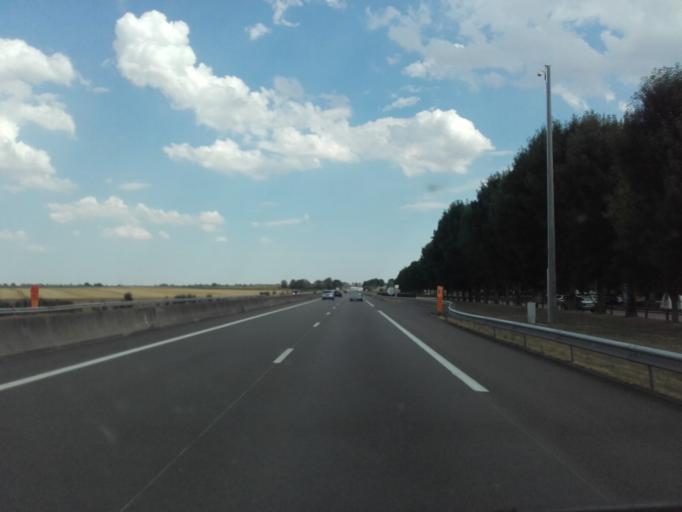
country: FR
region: Bourgogne
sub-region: Departement de la Cote-d'Or
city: Semur-en-Auxois
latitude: 47.4859
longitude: 4.1582
